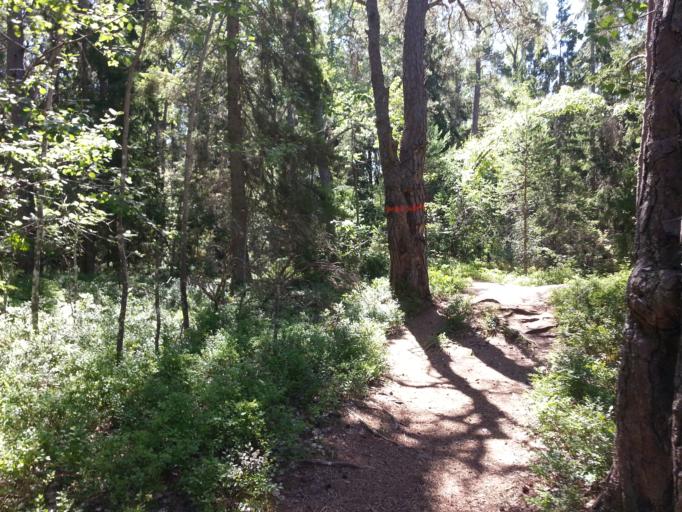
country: SE
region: Stockholm
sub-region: Tyreso Kommun
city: Bollmora
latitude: 59.2261
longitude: 18.2632
